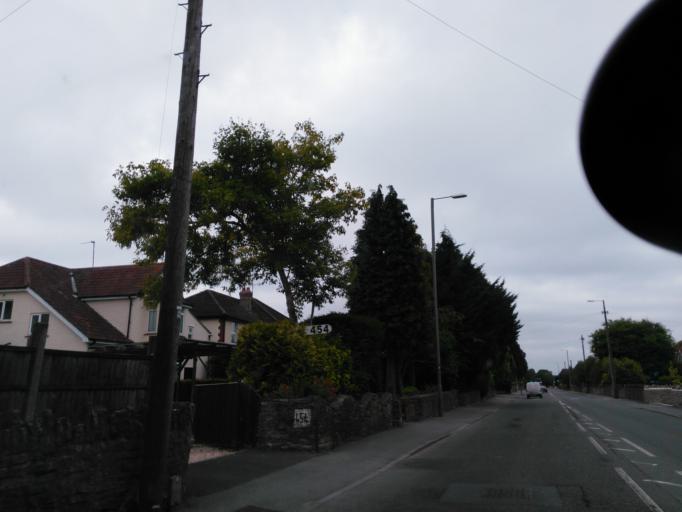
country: GB
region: England
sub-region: Bath and North East Somerset
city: Saltford
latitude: 51.4025
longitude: -2.4601
